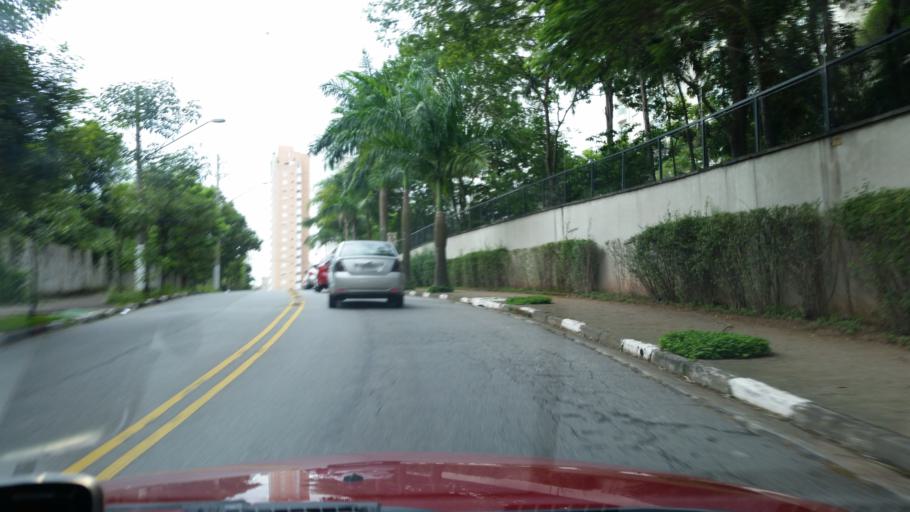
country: BR
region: Sao Paulo
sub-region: Taboao Da Serra
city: Taboao da Serra
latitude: -23.6317
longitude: -46.7343
